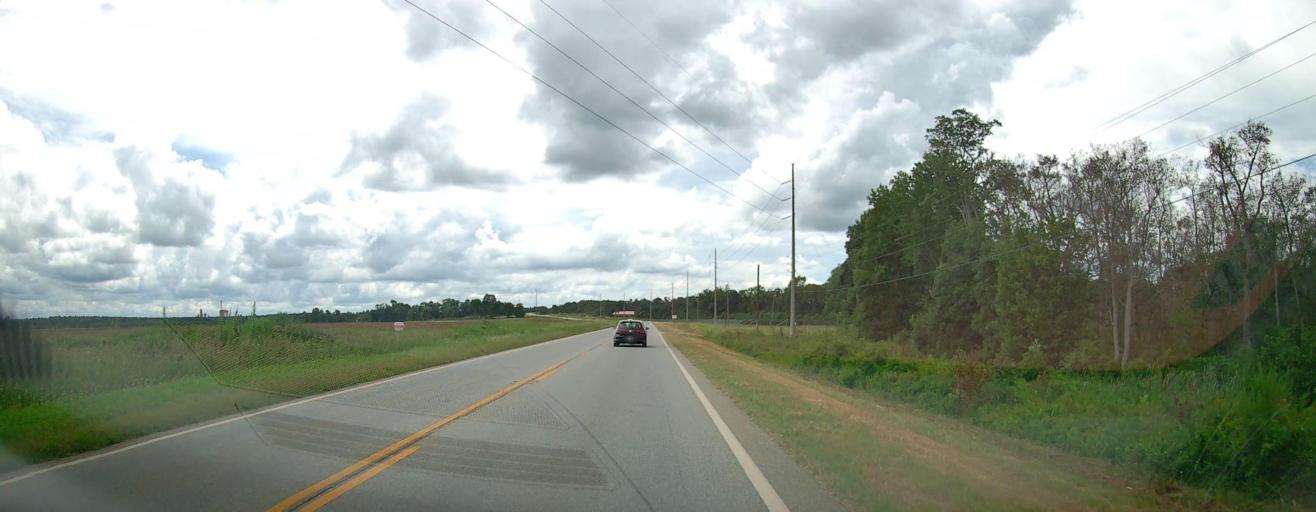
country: US
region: Georgia
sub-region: Macon County
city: Oglethorpe
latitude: 32.2833
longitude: -84.0595
